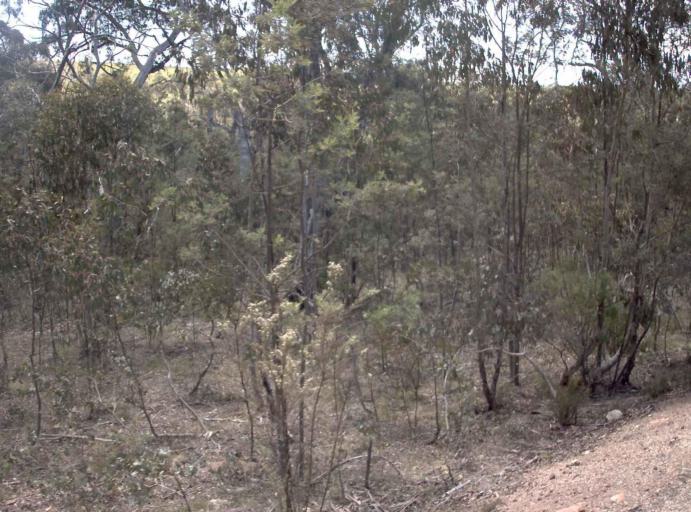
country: AU
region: New South Wales
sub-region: Snowy River
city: Jindabyne
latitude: -37.0710
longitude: 148.2819
